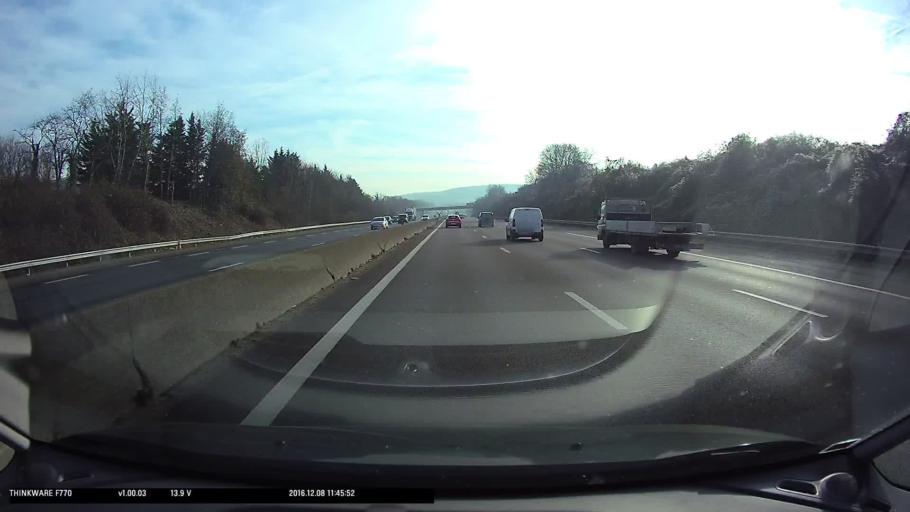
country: FR
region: Ile-de-France
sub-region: Departement du Val-d'Oise
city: Herblay
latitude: 49.0013
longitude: 2.1723
